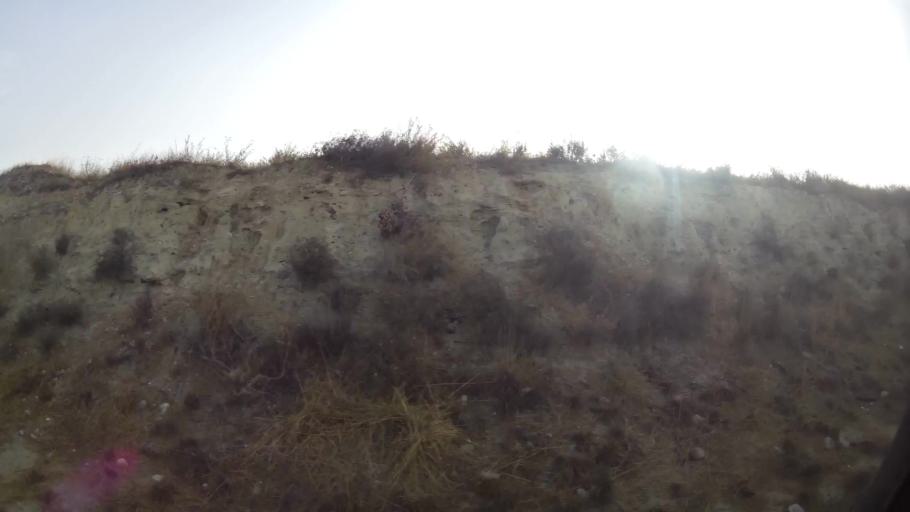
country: CY
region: Lefkosia
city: Dali
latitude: 35.0623
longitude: 33.3889
